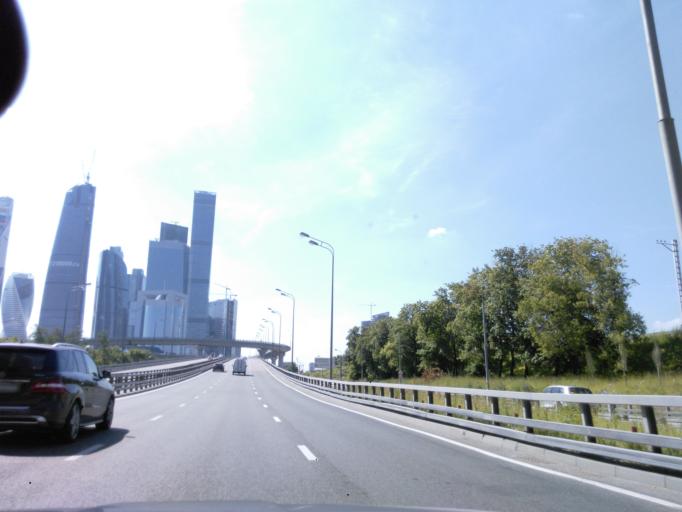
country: RU
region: Moskovskaya
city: Presnenskiy
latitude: 55.7580
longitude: 37.5260
